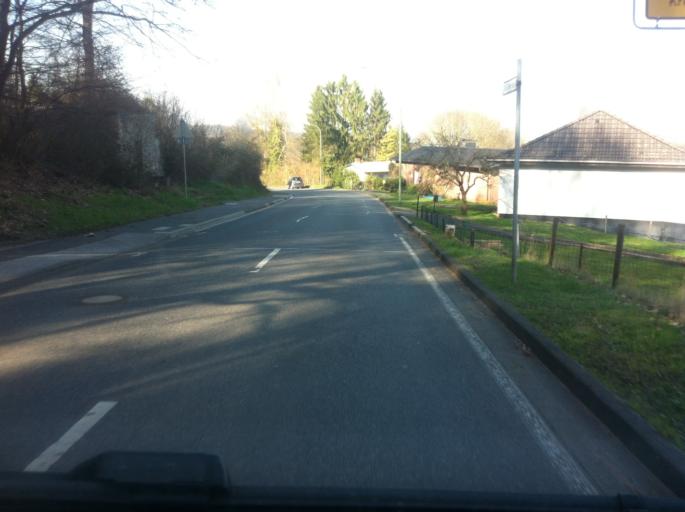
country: DE
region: North Rhine-Westphalia
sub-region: Regierungsbezirk Koln
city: Nideggen
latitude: 50.7129
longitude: 6.4675
